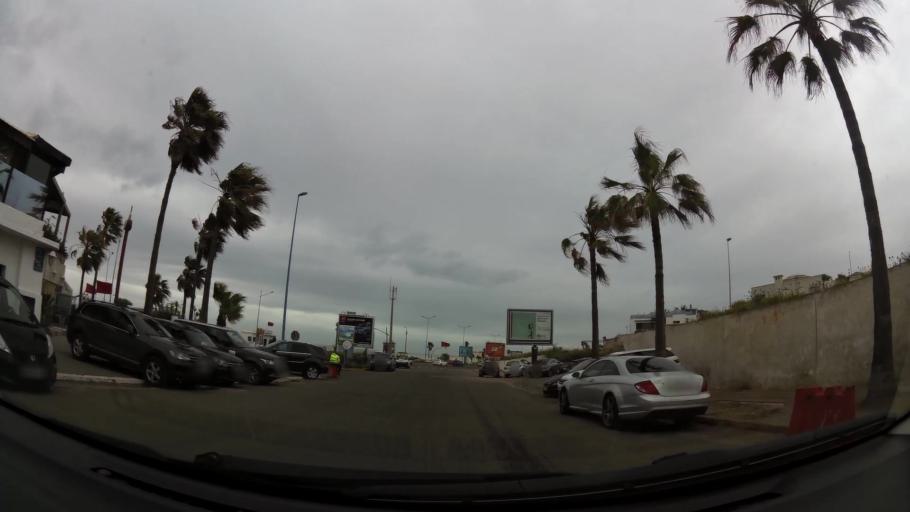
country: MA
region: Grand Casablanca
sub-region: Casablanca
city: Casablanca
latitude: 33.6015
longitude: -7.6603
